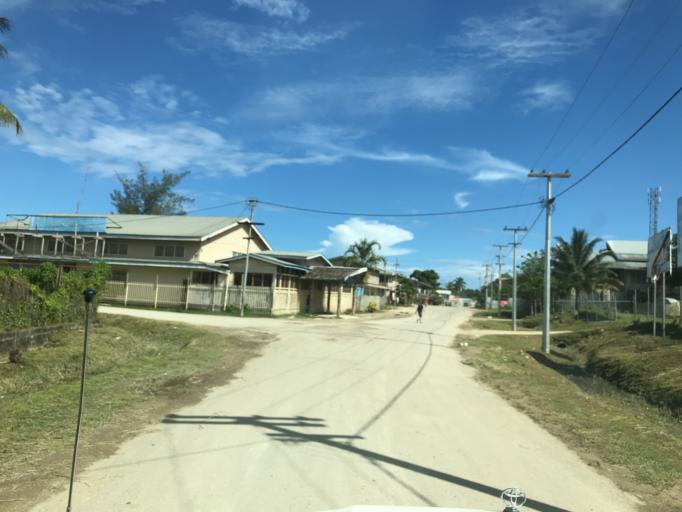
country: SB
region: Malaita
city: Auki
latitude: -8.7723
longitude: 160.6995
